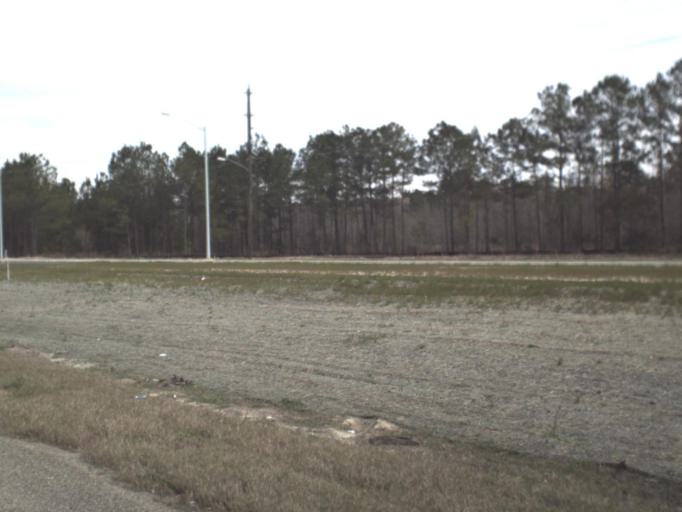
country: US
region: Florida
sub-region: Leon County
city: Tallahassee
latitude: 30.4261
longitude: -84.3528
